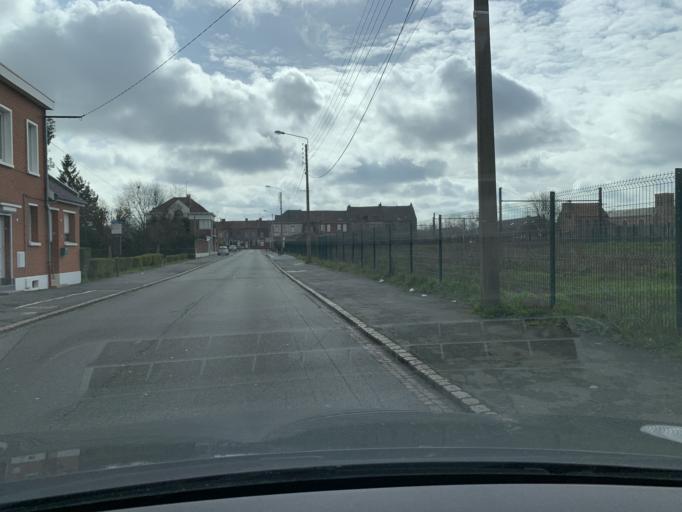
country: FR
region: Nord-Pas-de-Calais
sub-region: Departement du Nord
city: Flers-en-Escrebieux
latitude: 50.3962
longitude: 3.0862
